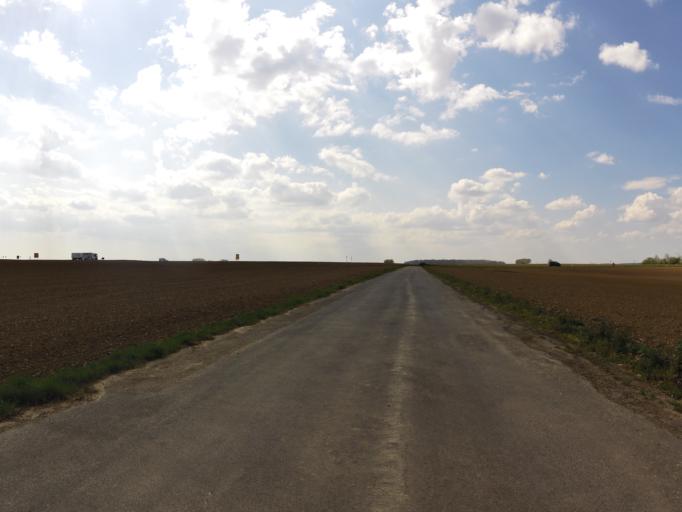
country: DE
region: Bavaria
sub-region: Regierungsbezirk Unterfranken
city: Giebelstadt
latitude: 49.6711
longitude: 9.9489
